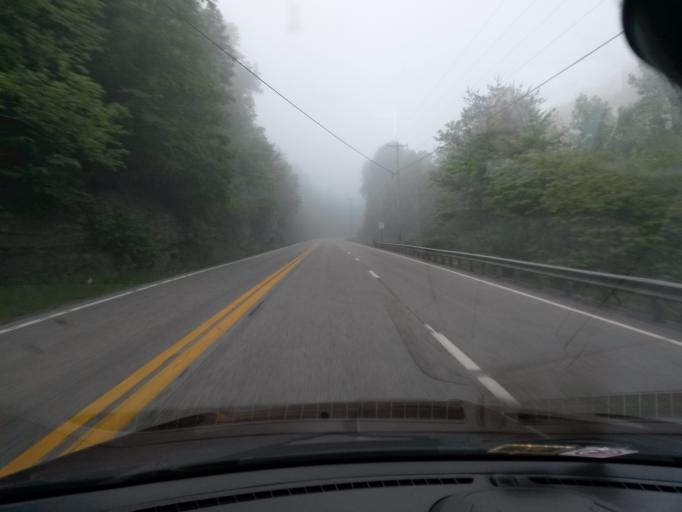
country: US
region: West Virginia
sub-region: McDowell County
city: Welch
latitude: 37.4962
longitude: -81.5393
